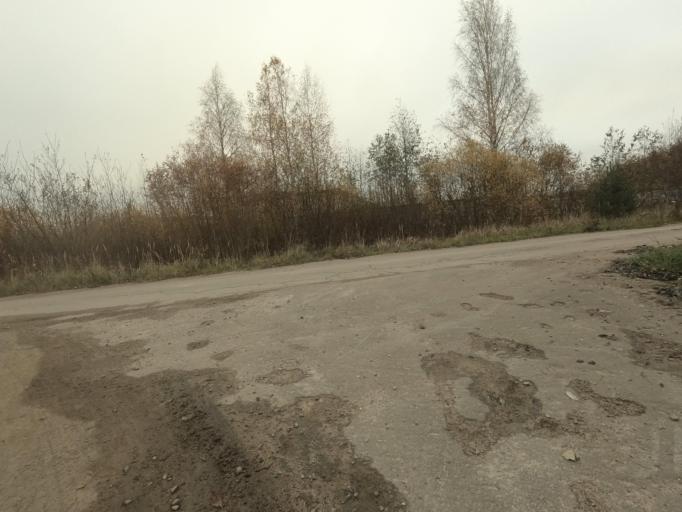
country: RU
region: Leningrad
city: Kirovsk
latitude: 59.8566
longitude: 30.9870
